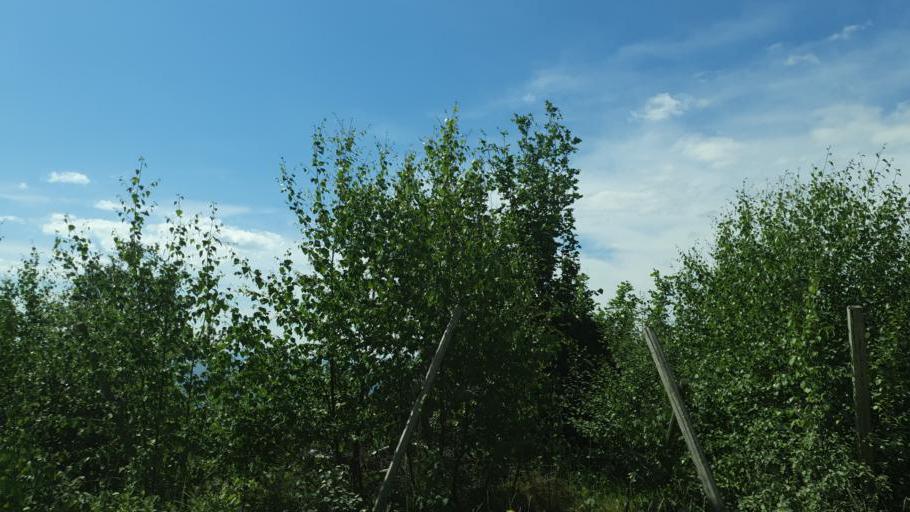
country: NO
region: Nord-Trondelag
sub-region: Leksvik
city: Leksvik
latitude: 63.6779
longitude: 10.6571
